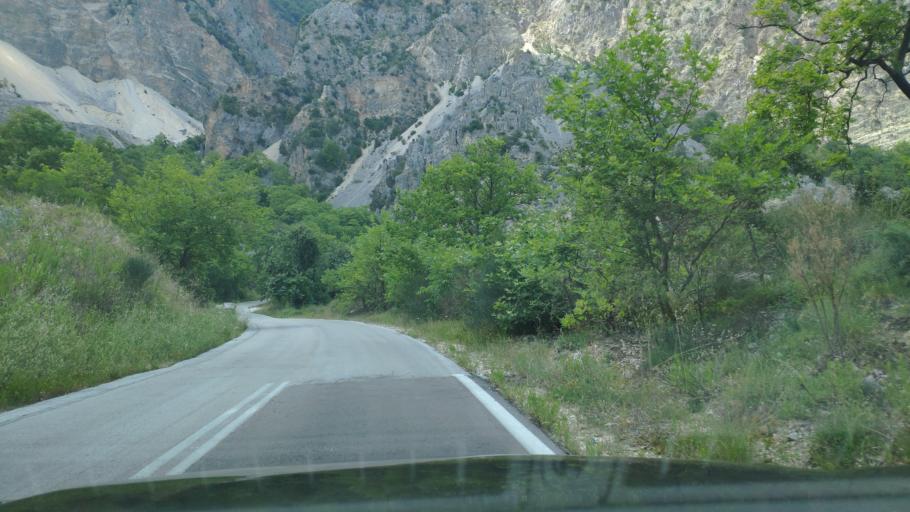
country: GR
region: Epirus
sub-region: Nomos Artas
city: Agios Dimitrios
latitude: 39.3442
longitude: 21.0056
